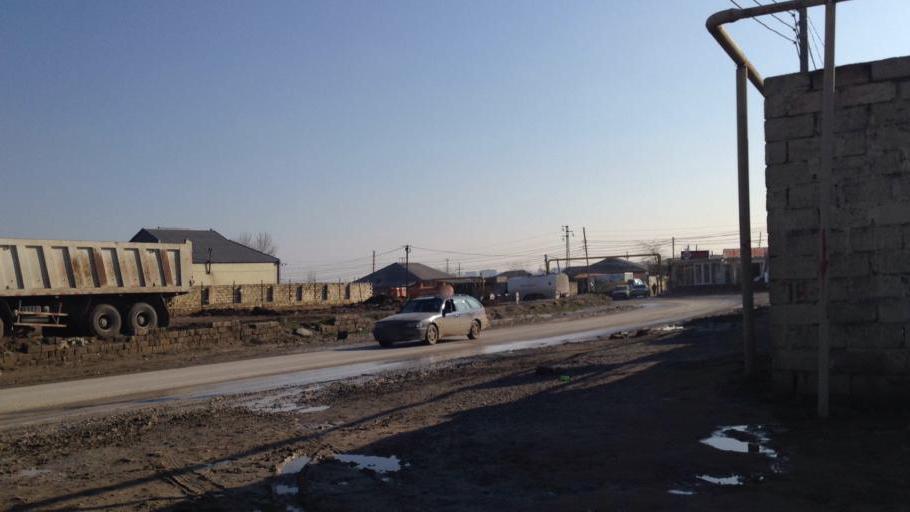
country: AZ
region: Baki
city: Sabuncu
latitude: 40.4491
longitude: 49.9314
